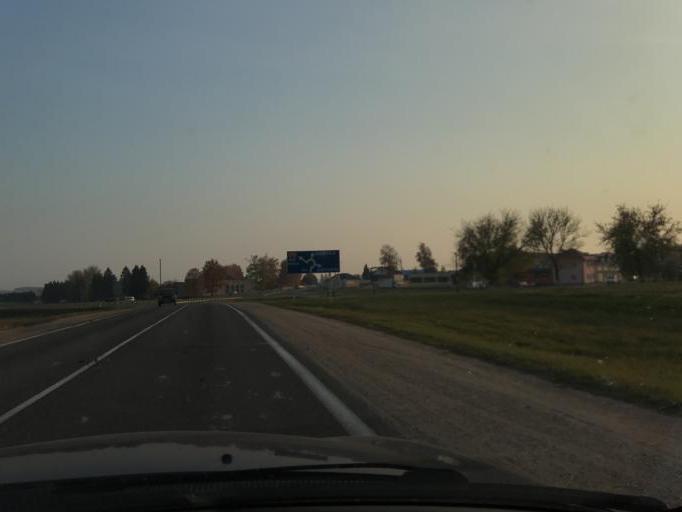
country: BY
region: Grodnenskaya
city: Karelichy
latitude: 53.5597
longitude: 26.1519
